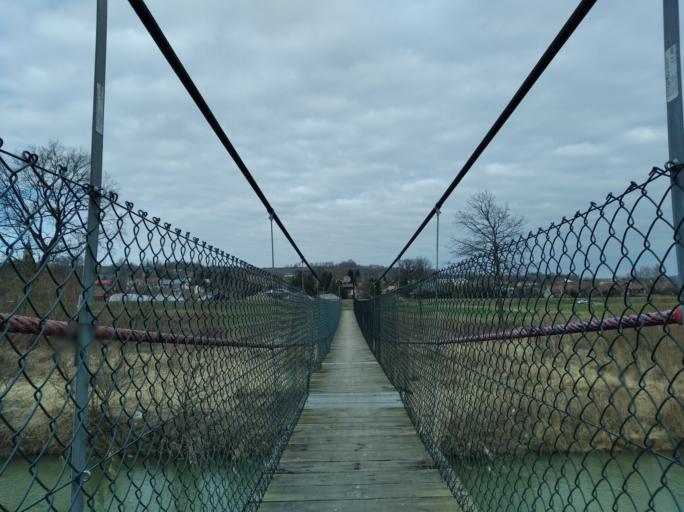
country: PL
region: Subcarpathian Voivodeship
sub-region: Powiat strzyzowski
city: Wysoka Strzyzowska
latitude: 49.8735
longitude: 21.7220
